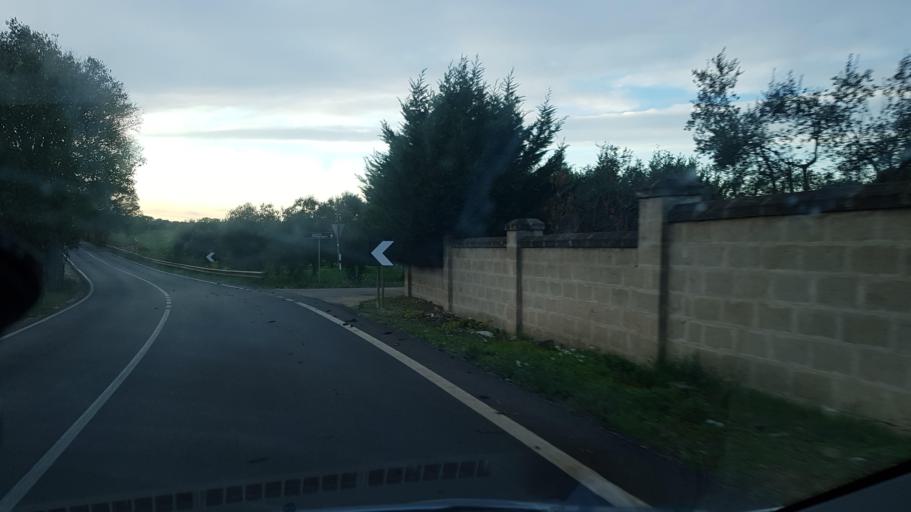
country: IT
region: Apulia
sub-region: Provincia di Brindisi
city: San Michele Salentino
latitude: 40.6468
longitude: 17.6239
